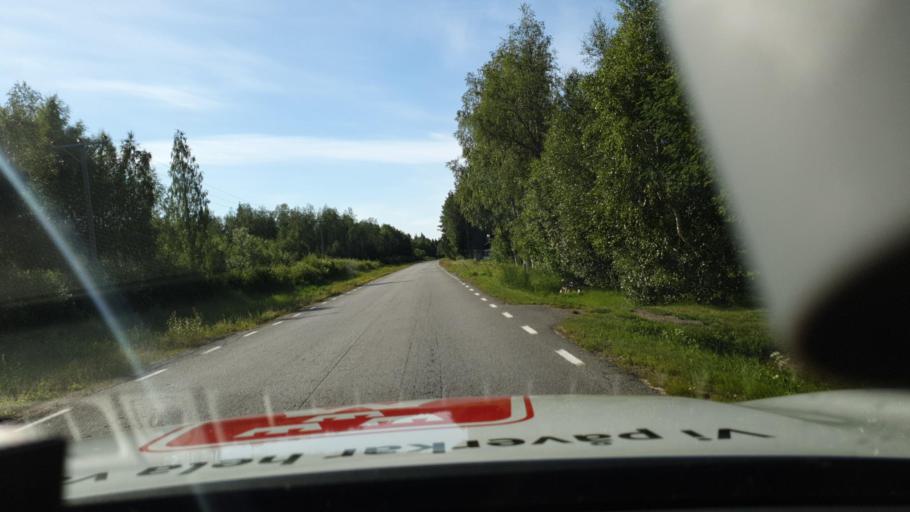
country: SE
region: Norrbotten
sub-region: Kalix Kommun
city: Toere
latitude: 65.8917
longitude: 22.6416
